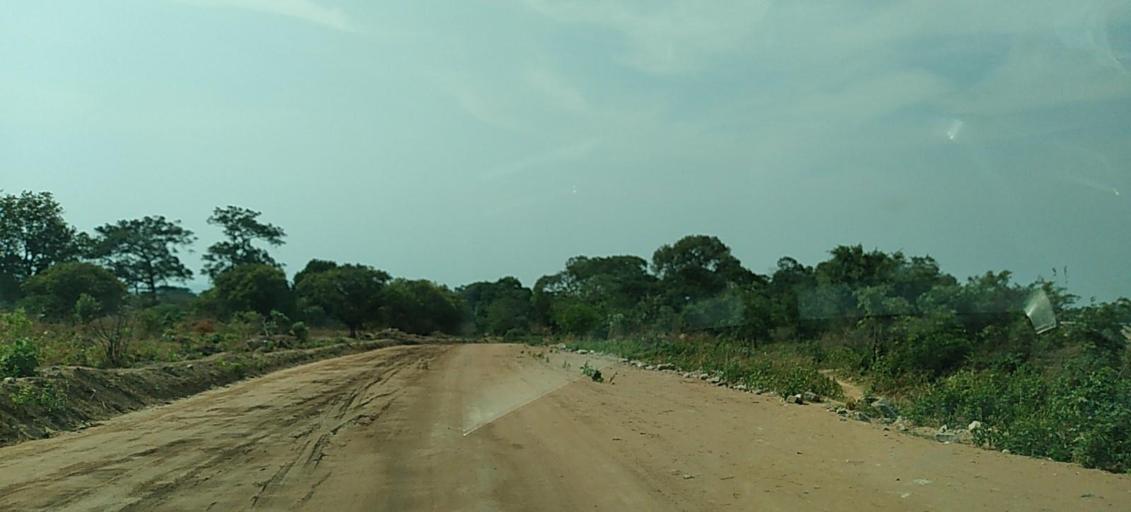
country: ZM
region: Copperbelt
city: Chililabombwe
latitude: -12.2952
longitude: 27.7623
